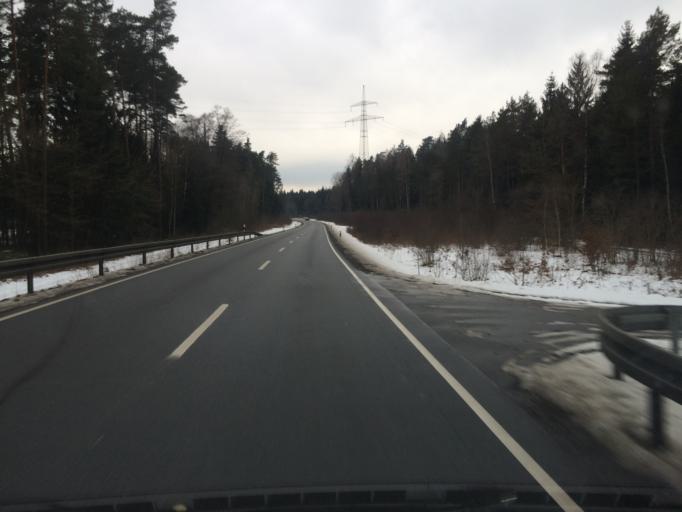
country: DE
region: Bavaria
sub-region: Upper Palatinate
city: Teublitz
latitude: 49.2192
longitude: 12.1175
